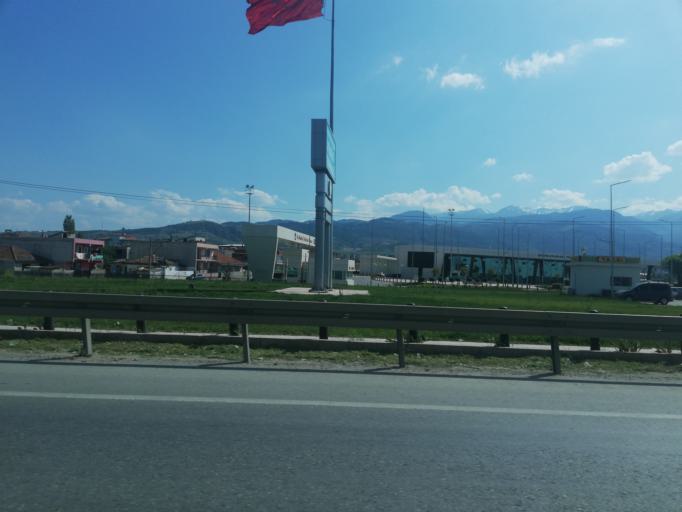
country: TR
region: Manisa
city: Alasehir
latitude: 38.3590
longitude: 28.5391
